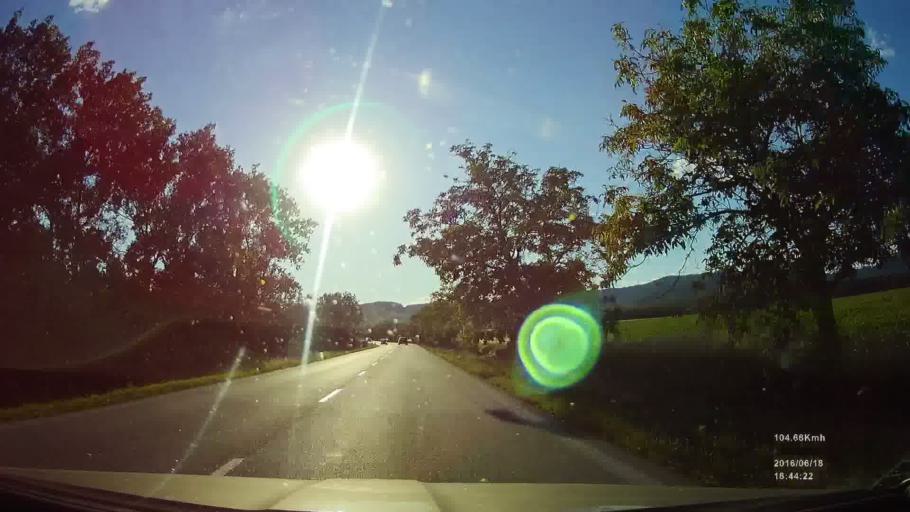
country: SK
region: Kosicky
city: Secovce
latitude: 48.7287
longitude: 21.5971
